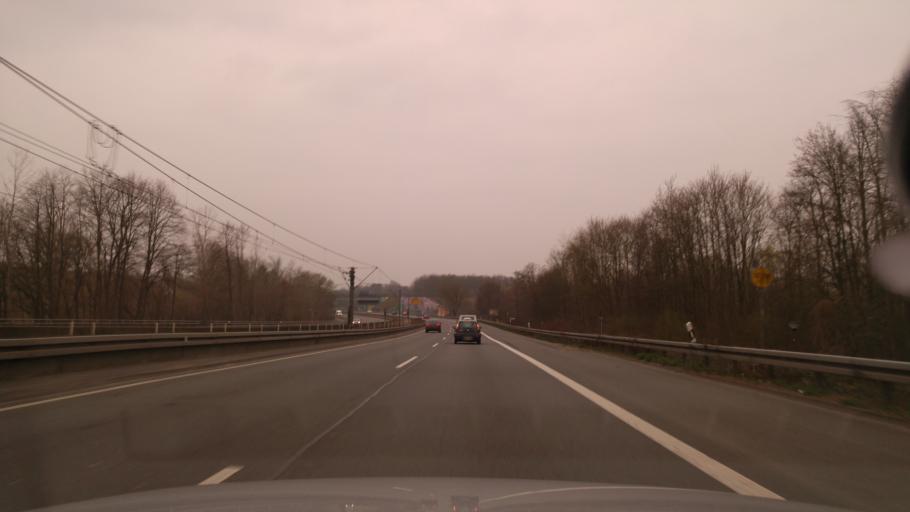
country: DE
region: North Rhine-Westphalia
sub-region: Regierungsbezirk Arnsberg
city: Dortmund
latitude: 51.4898
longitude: 7.4671
